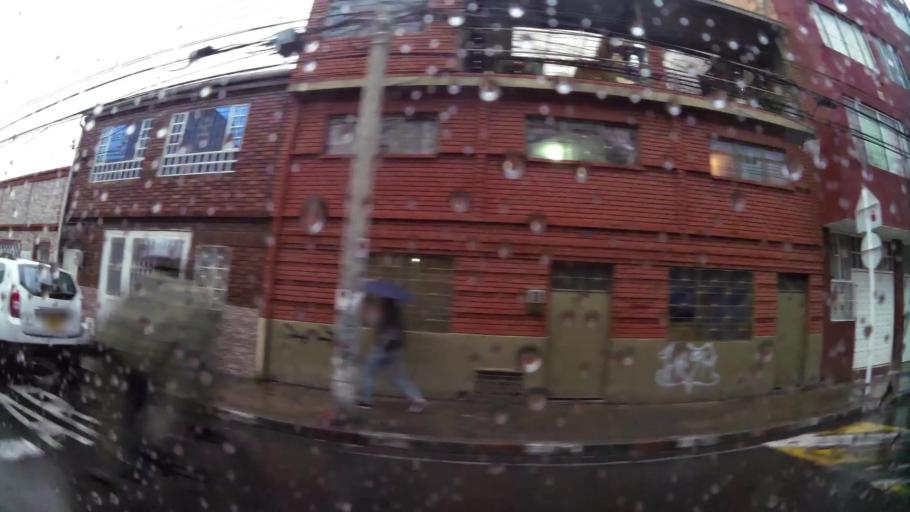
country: CO
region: Bogota D.C.
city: Bogota
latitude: 4.5873
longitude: -74.1367
